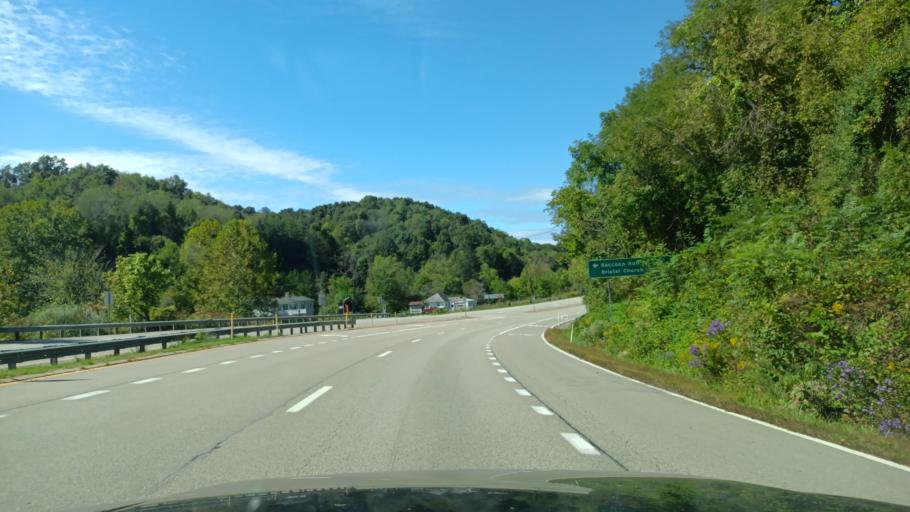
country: US
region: West Virginia
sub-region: Harrison County
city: Salem
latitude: 39.2880
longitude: -80.5222
